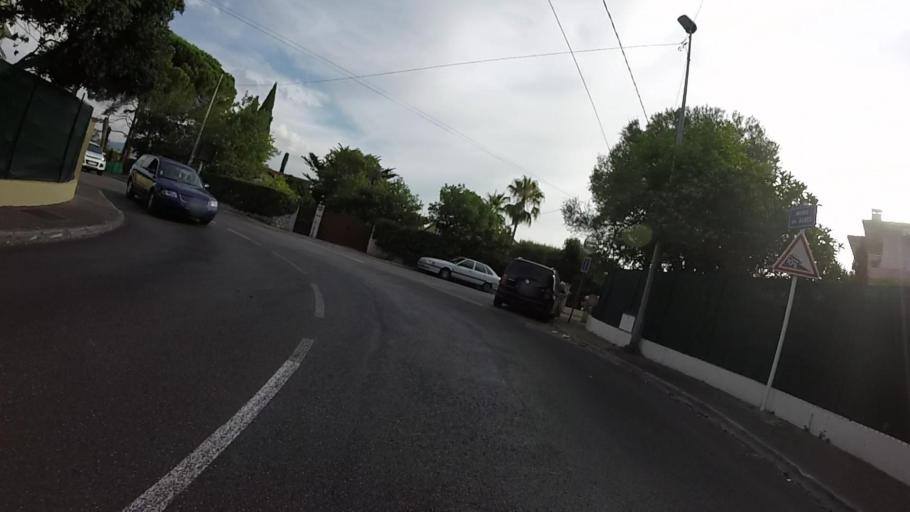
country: FR
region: Provence-Alpes-Cote d'Azur
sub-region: Departement des Alpes-Maritimes
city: Antibes
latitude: 43.5889
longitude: 7.1065
